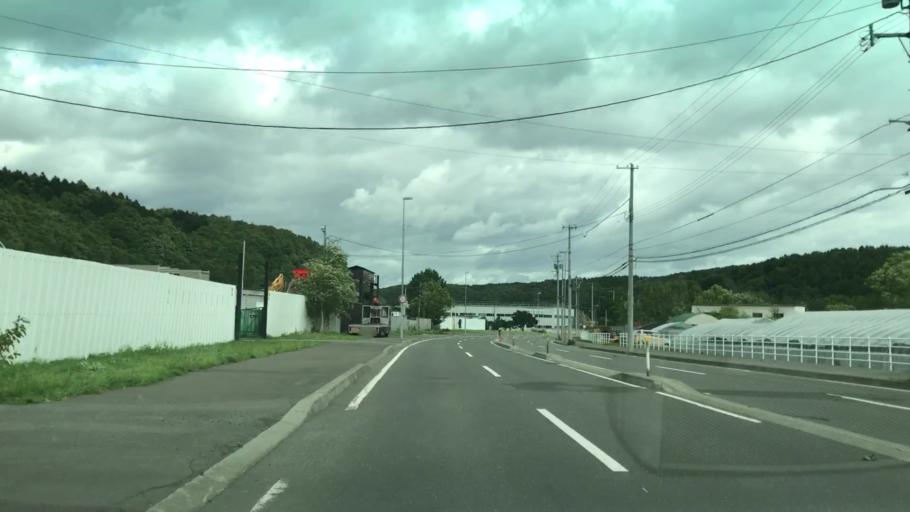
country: JP
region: Hokkaido
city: Kitahiroshima
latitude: 42.9563
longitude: 141.4541
